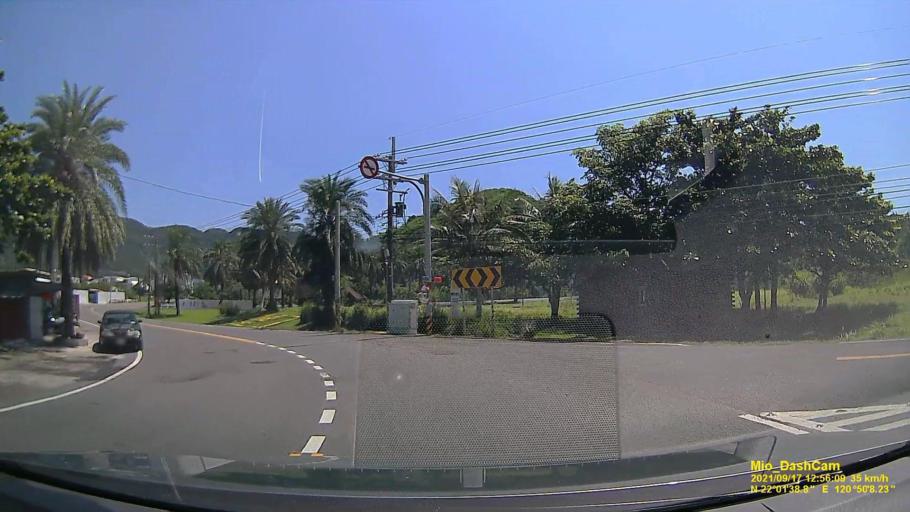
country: TW
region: Taiwan
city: Hengchun
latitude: 22.0274
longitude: 120.8356
